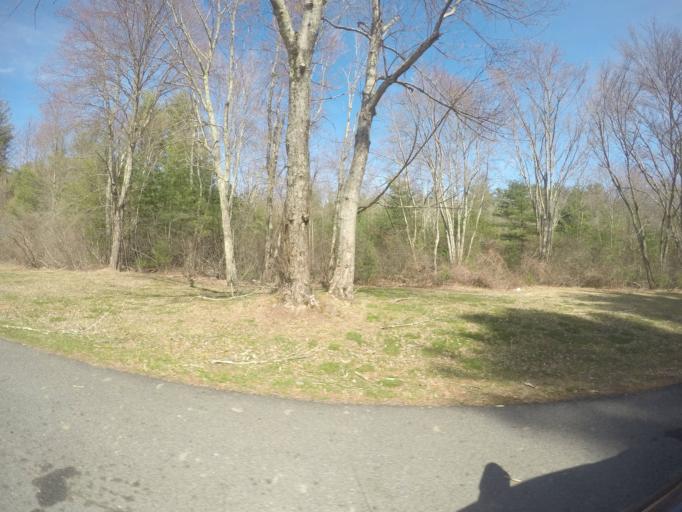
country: US
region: Massachusetts
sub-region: Bristol County
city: Easton
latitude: 42.0255
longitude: -71.0750
